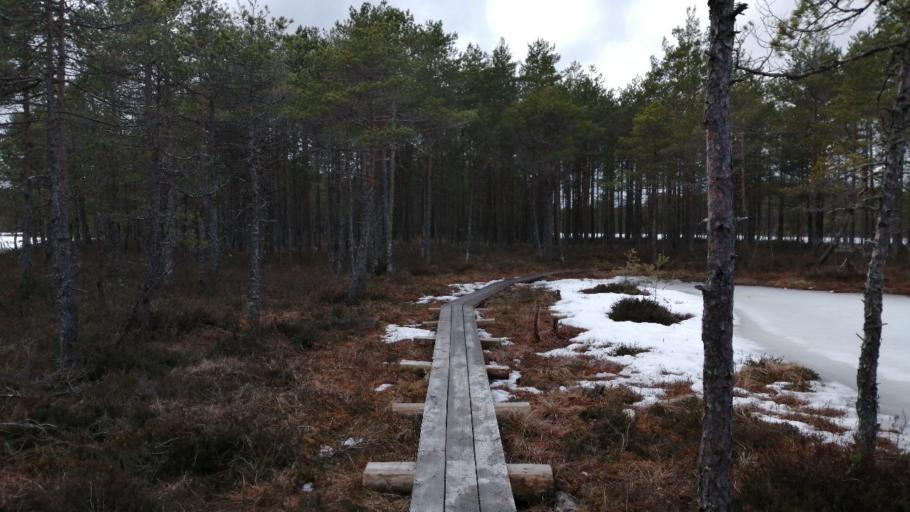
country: EE
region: Ida-Virumaa
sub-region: Kohtla-Nomme vald
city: Kohtla-Nomme
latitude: 59.1717
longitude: 27.2826
